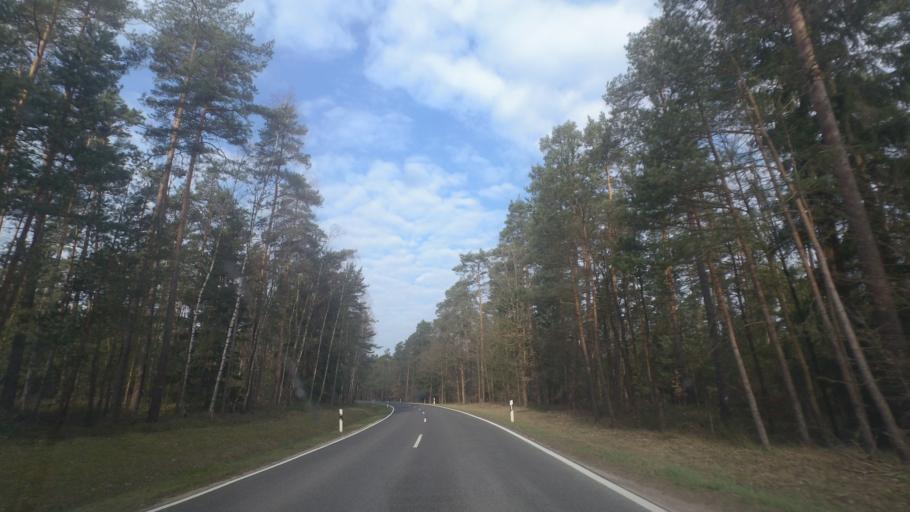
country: DE
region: Bavaria
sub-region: Regierungsbezirk Mittelfranken
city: Winkelhaid
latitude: 49.4072
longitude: 11.3078
